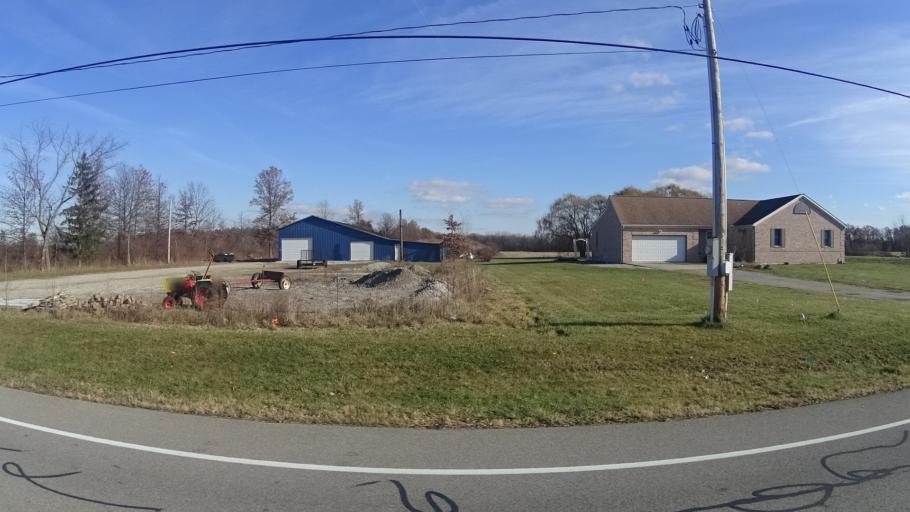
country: US
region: Ohio
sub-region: Lorain County
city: Eaton Estates
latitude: 41.3023
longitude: -81.9817
